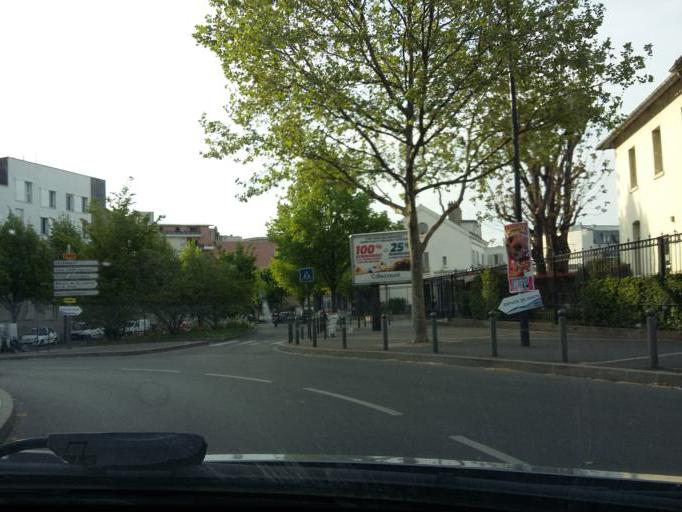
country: FR
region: Ile-de-France
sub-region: Departement du Val-d'Oise
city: Argenteuil
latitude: 48.9435
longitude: 2.2558
